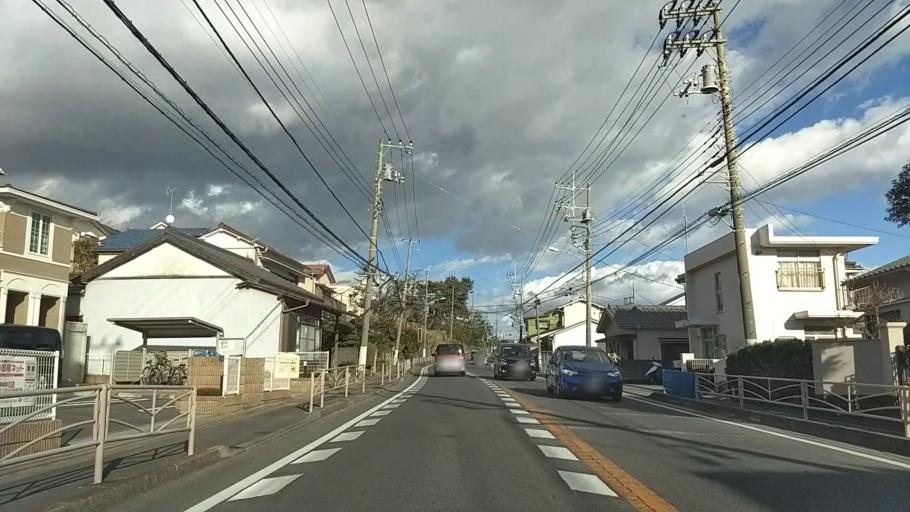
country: JP
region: Kanagawa
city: Ninomiya
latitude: 35.2852
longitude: 139.2279
